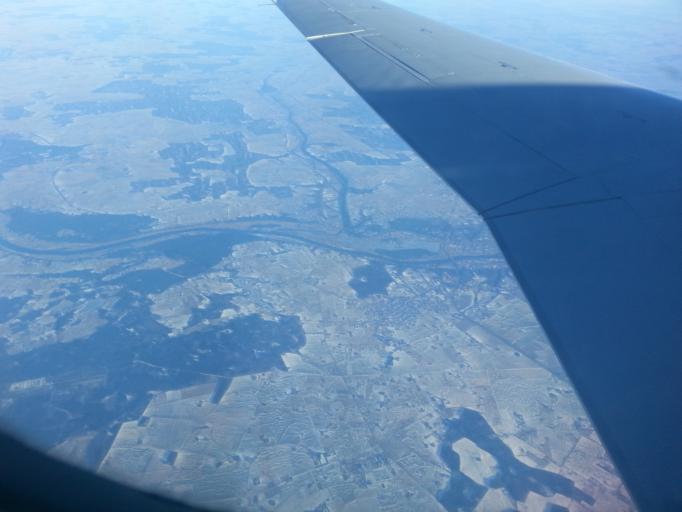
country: LT
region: Kauno apskritis
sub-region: Kauno rajonas
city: Mastaiciai
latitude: 54.7888
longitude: 23.7264
